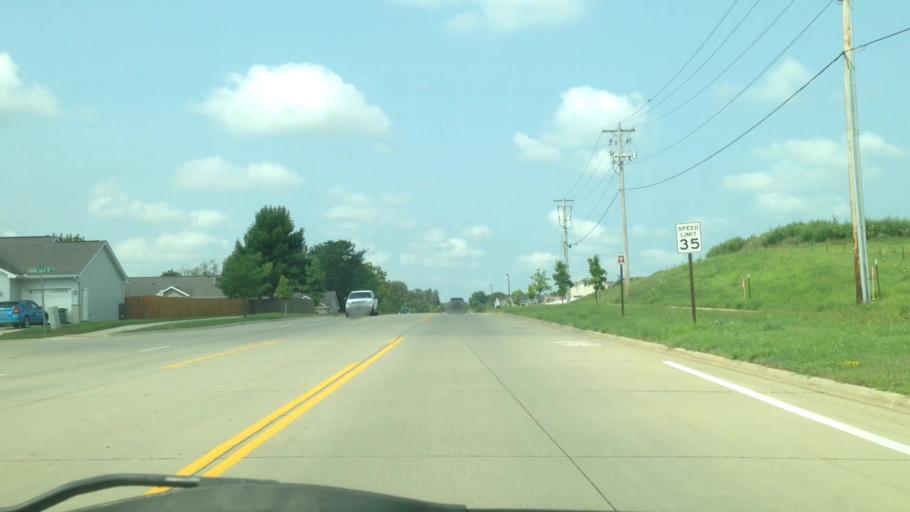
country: US
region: Iowa
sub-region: Linn County
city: Cedar Rapids
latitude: 41.9456
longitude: -91.6971
